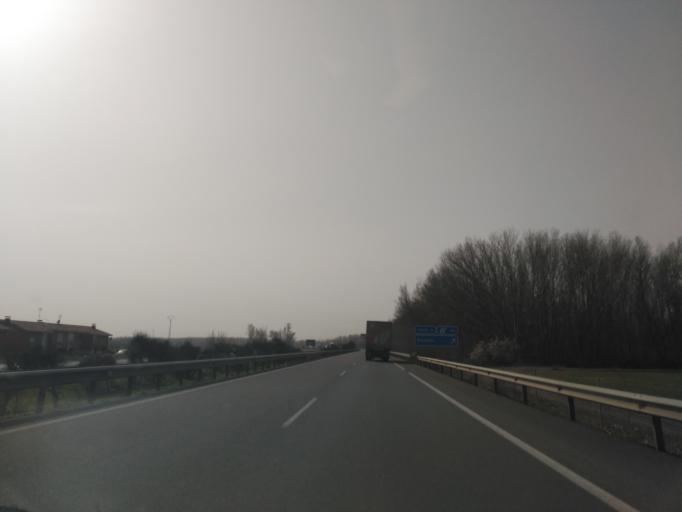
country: ES
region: Castille and Leon
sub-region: Provincia de Palencia
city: Duenas
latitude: 41.8979
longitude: -4.5199
